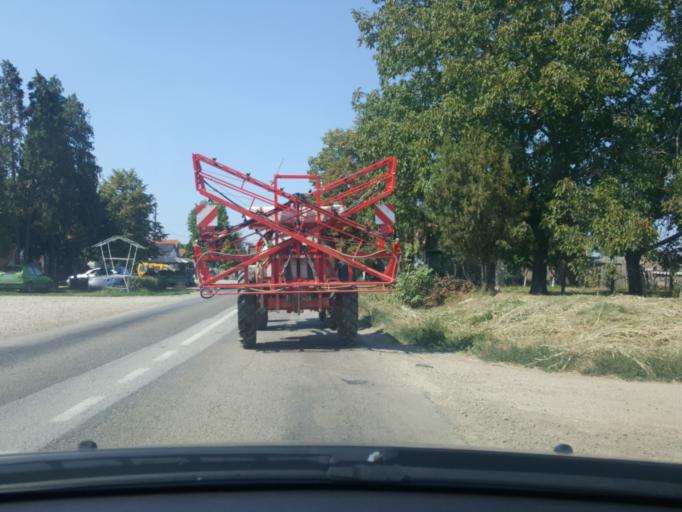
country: RS
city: Hrtkovci
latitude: 44.8679
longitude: 19.7709
